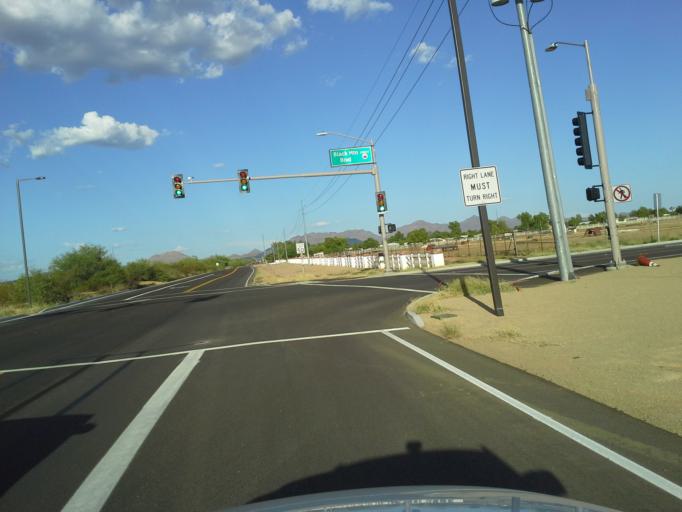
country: US
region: Arizona
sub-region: Maricopa County
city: Cave Creek
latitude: 33.6987
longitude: -112.0057
